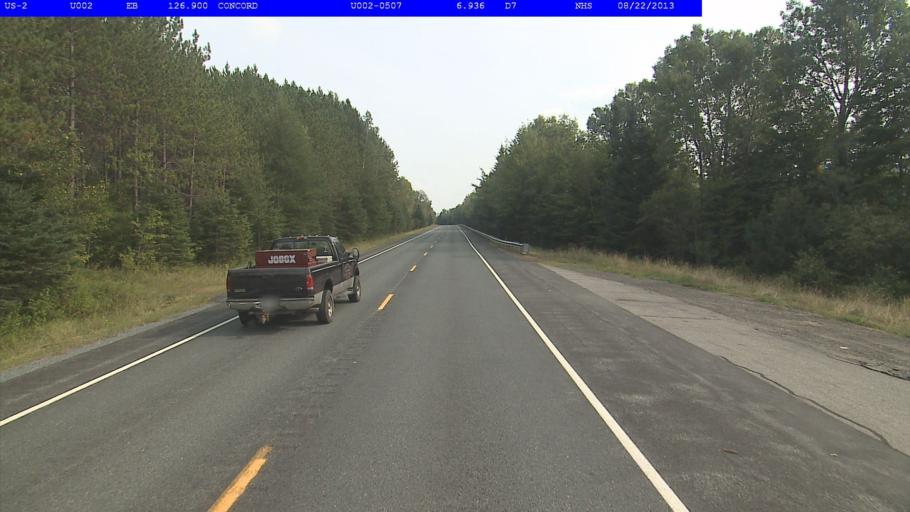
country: US
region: New Hampshire
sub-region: Grafton County
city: Littleton
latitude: 44.4600
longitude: -71.8321
